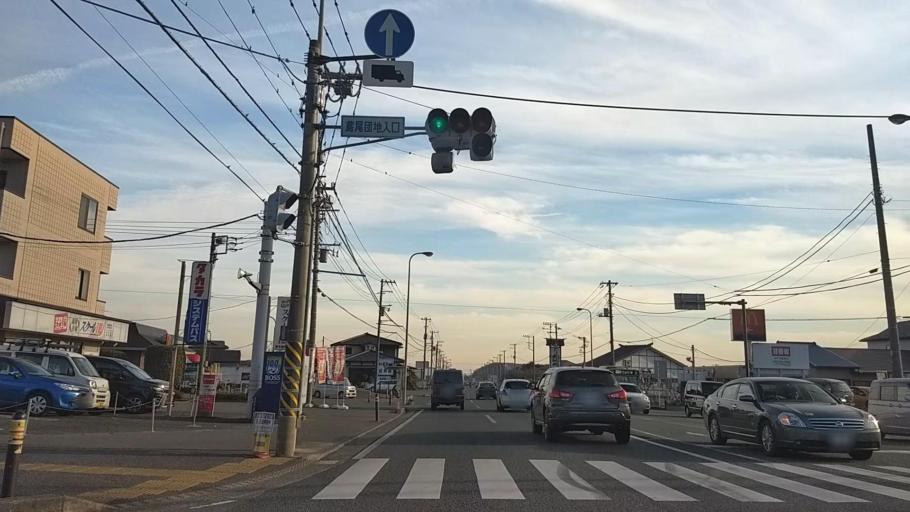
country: JP
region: Kanagawa
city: Atsugi
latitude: 35.4895
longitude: 139.3241
